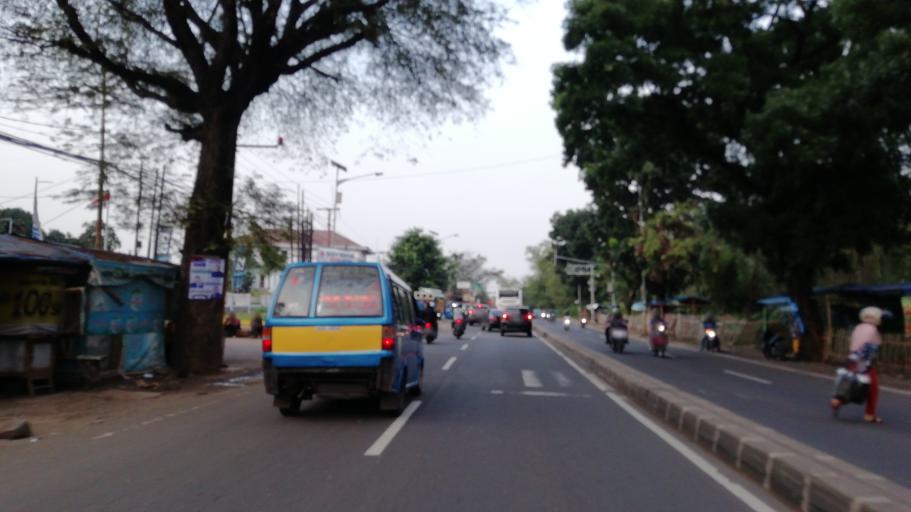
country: ID
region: West Java
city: Depok
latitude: -6.4124
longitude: 106.8606
